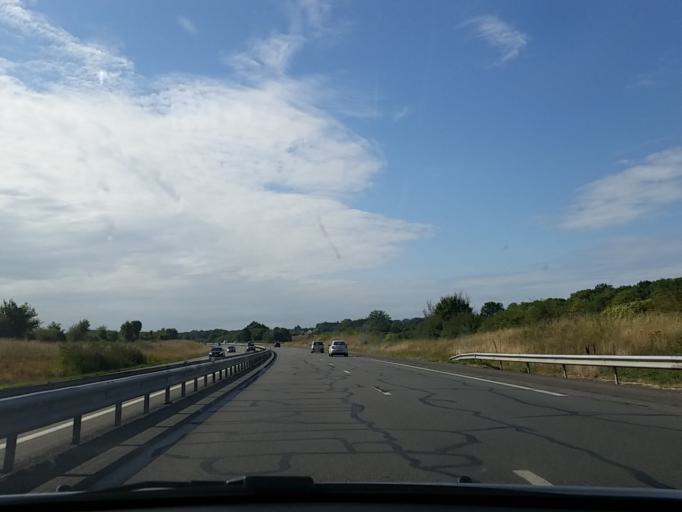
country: FR
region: Centre
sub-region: Departement du Cher
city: Orval
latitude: 46.7743
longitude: 2.4062
